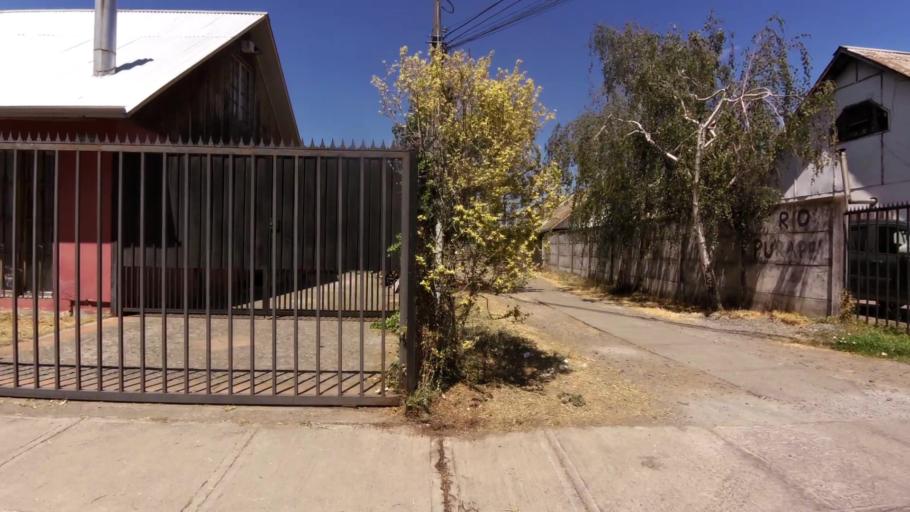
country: CL
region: Maule
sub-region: Provincia de Curico
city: Curico
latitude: -34.9821
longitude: -71.2162
